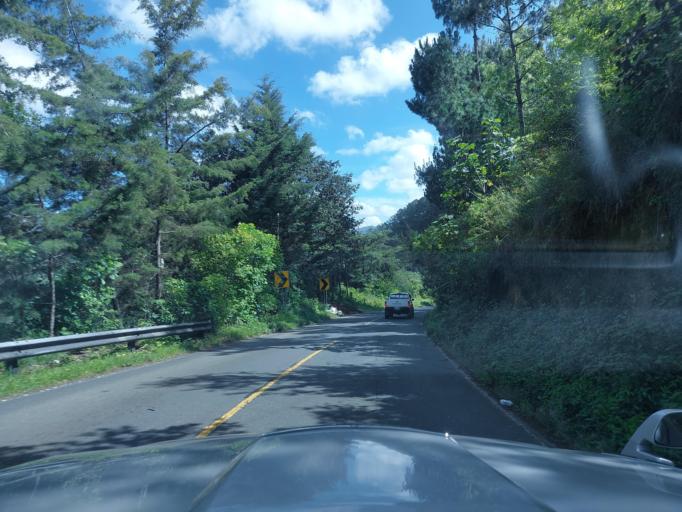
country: GT
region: Chimaltenango
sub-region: Municipio de Santa Cruz Balanya
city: Santa Cruz Balanya
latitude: 14.6822
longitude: -90.8958
